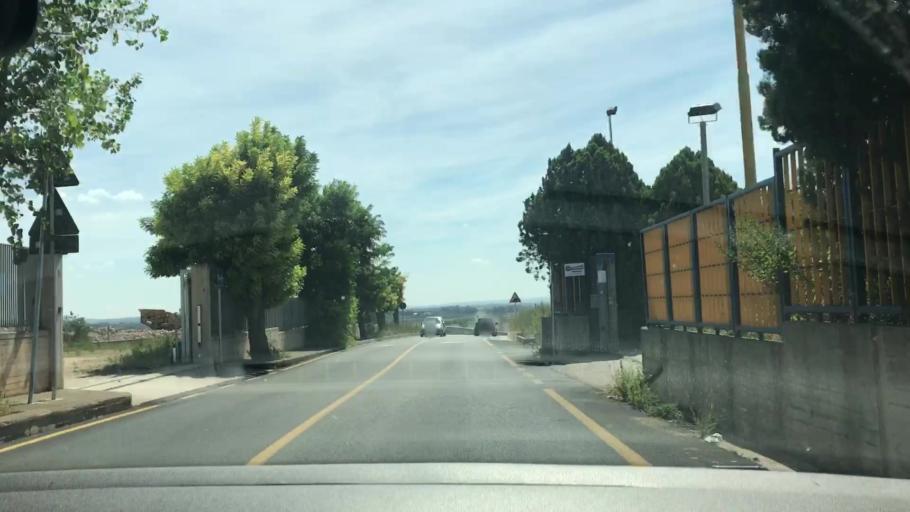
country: IT
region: Apulia
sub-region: Provincia di Bari
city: Altamura
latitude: 40.8110
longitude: 16.5546
